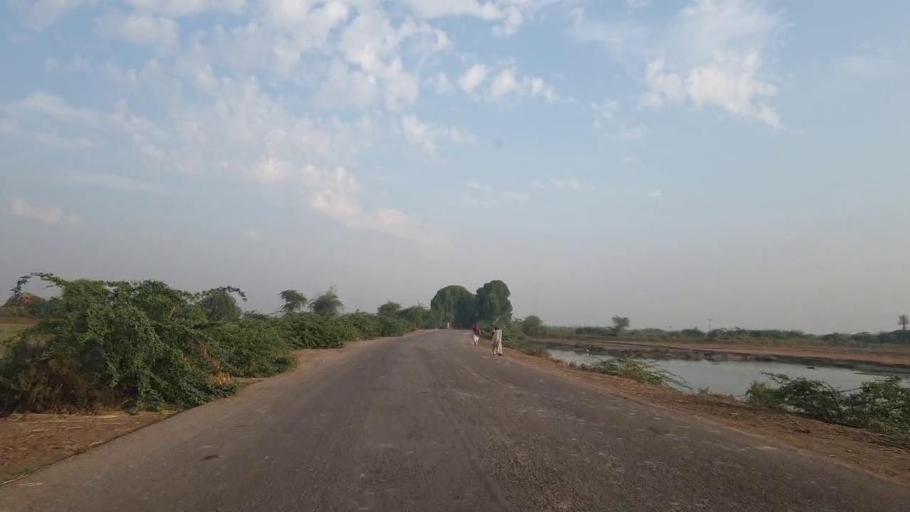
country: PK
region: Sindh
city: Tando Bago
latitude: 24.7254
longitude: 68.9426
